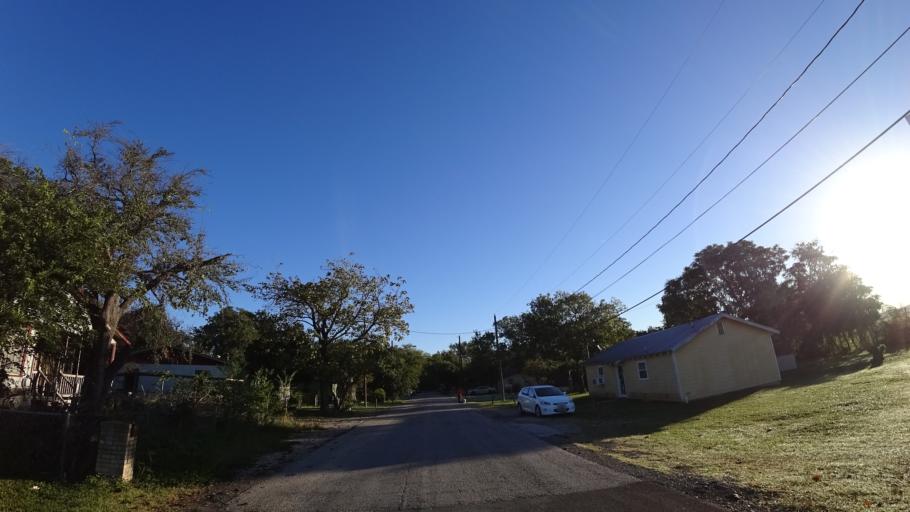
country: US
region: Texas
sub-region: Travis County
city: Hornsby Bend
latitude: 30.2028
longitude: -97.6378
